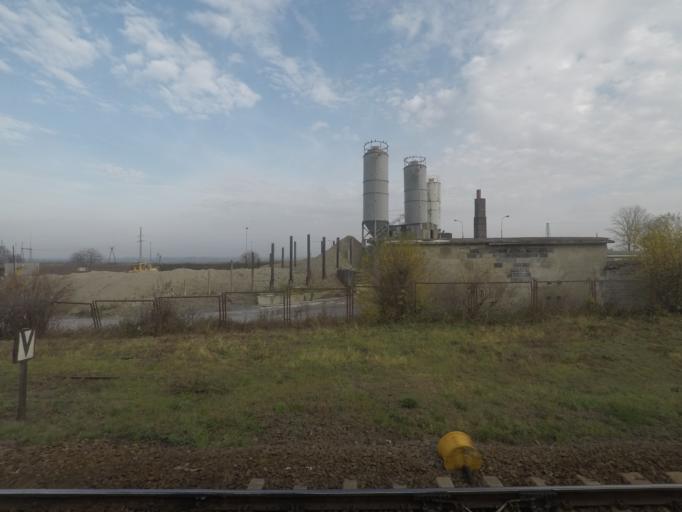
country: PL
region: Subcarpathian Voivodeship
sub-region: Powiat jaroslawski
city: Radymno
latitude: 49.9340
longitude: 22.8369
